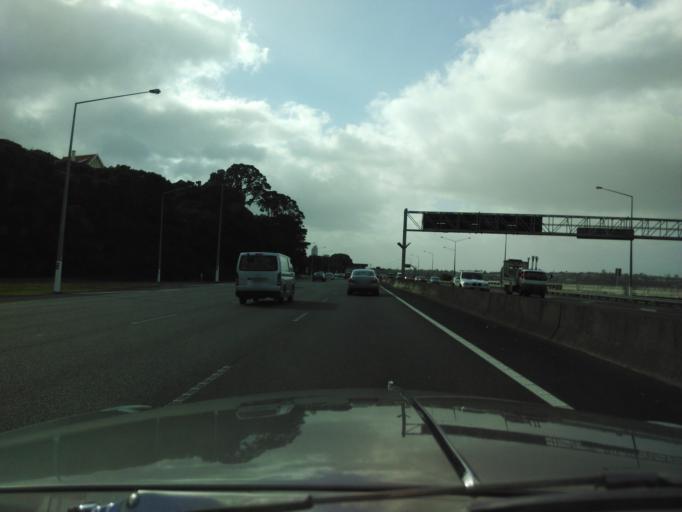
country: NZ
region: Auckland
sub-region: Auckland
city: North Shore
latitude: -36.8116
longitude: 174.7540
